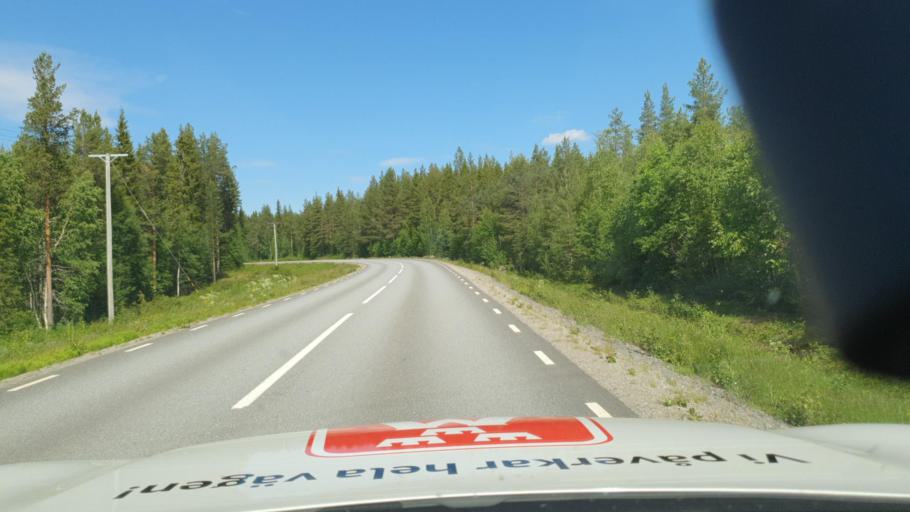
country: SE
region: Vaesterbotten
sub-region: Skelleftea Kommun
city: Langsele
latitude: 64.7484
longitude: 20.3492
